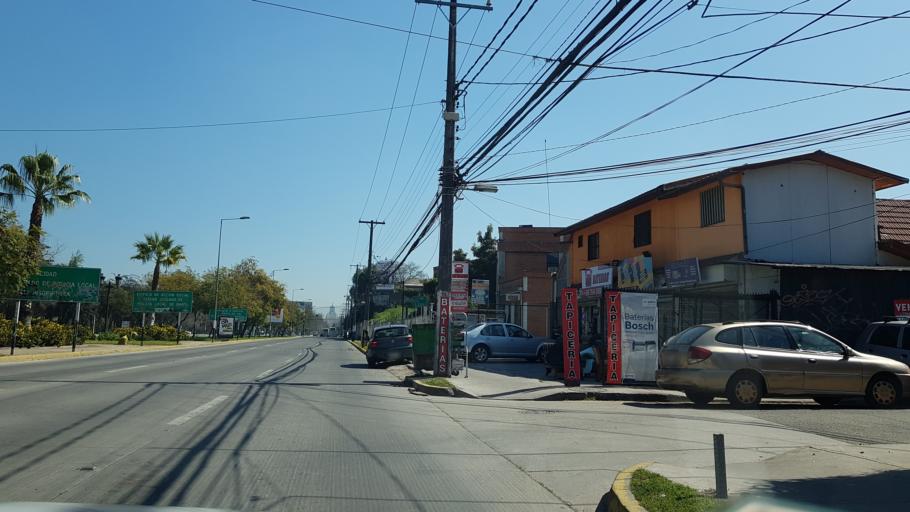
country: CL
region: Santiago Metropolitan
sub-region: Provincia de Santiago
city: Lo Prado
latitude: -33.5102
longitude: -70.7448
